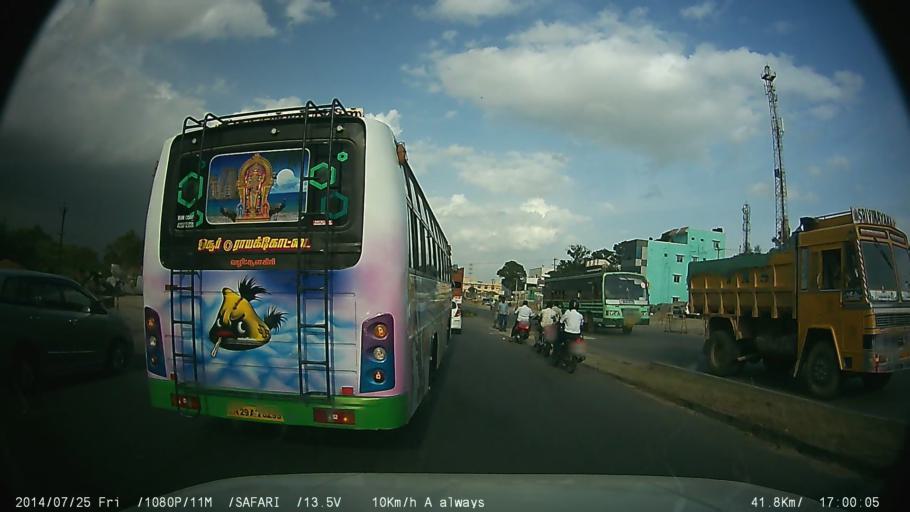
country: IN
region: Tamil Nadu
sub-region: Krishnagiri
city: Hosur
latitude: 12.7268
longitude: 77.8501
